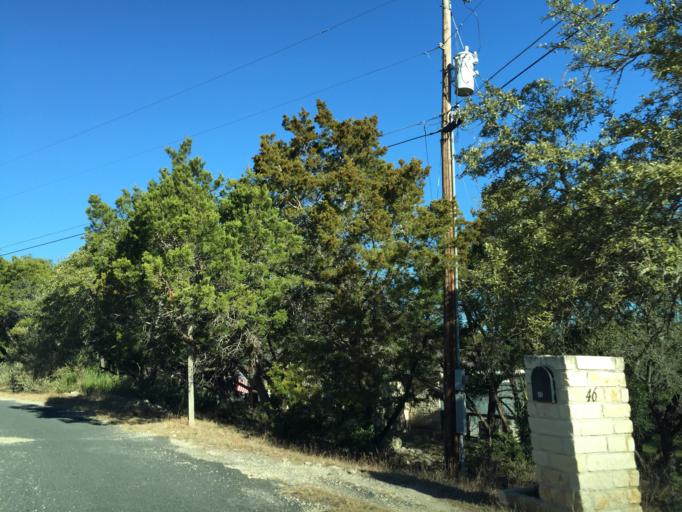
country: US
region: Texas
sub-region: Hays County
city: Woodcreek
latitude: 30.0107
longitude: -98.1152
